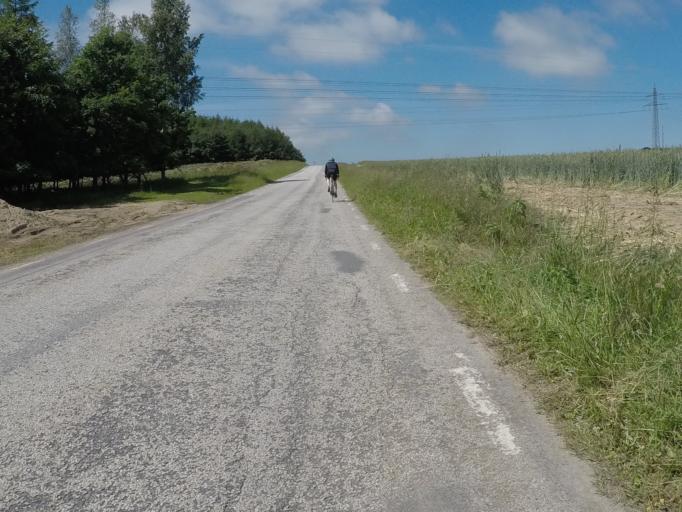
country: SE
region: Skane
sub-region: Svedala Kommun
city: Svedala
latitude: 55.5445
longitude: 13.1768
